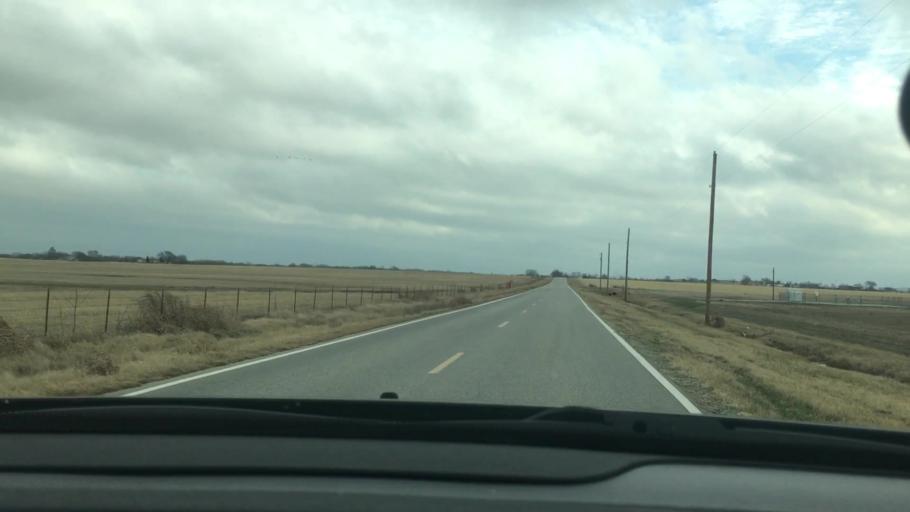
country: US
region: Oklahoma
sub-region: Bryan County
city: Durant
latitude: 34.0887
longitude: -96.4696
